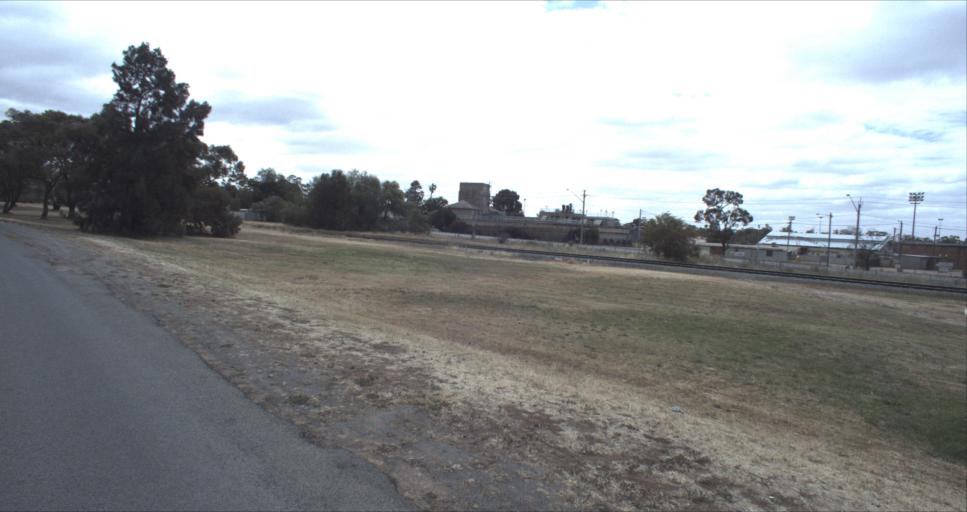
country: AU
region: New South Wales
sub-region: Leeton
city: Leeton
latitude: -34.5592
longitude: 146.4017
